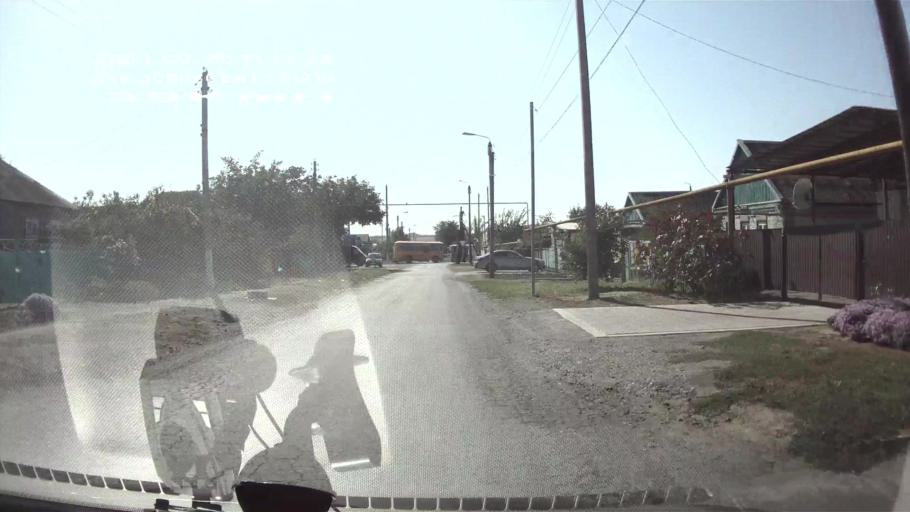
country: RU
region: Rostov
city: Gigant
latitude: 46.5090
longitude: 41.3412
